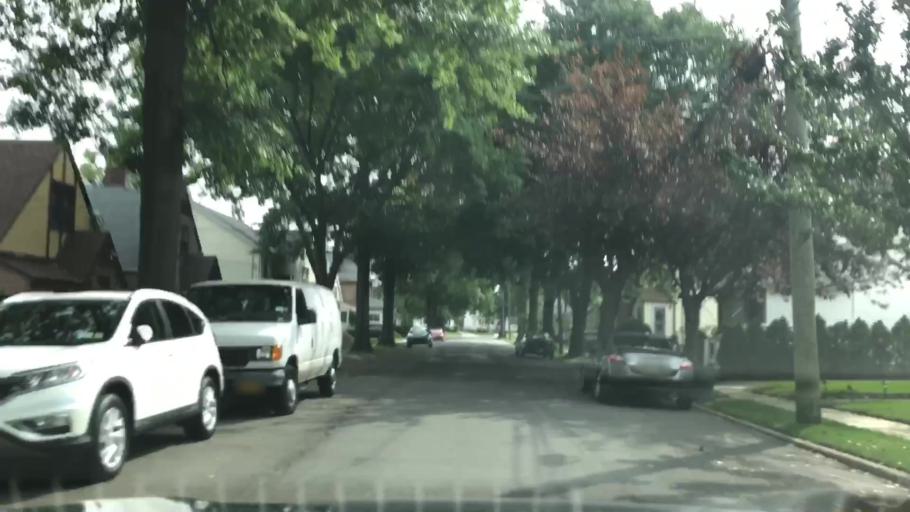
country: US
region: New York
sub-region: Nassau County
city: Floral Park
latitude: 40.7288
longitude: -73.6975
